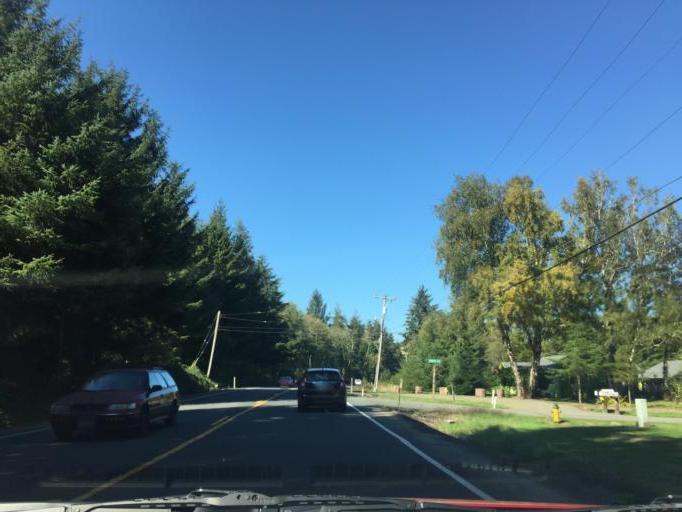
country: US
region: Oregon
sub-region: Clatsop County
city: Cannon Beach
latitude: 45.9056
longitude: -123.8785
